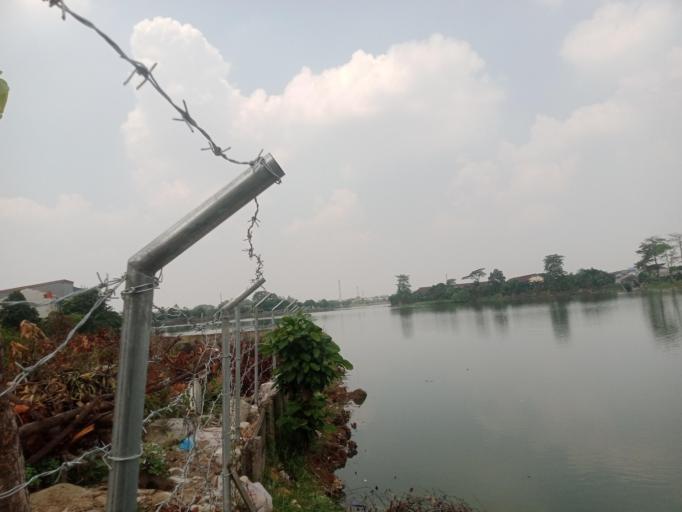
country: ID
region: West Java
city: Sepatan
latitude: -6.1608
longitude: 106.5820
